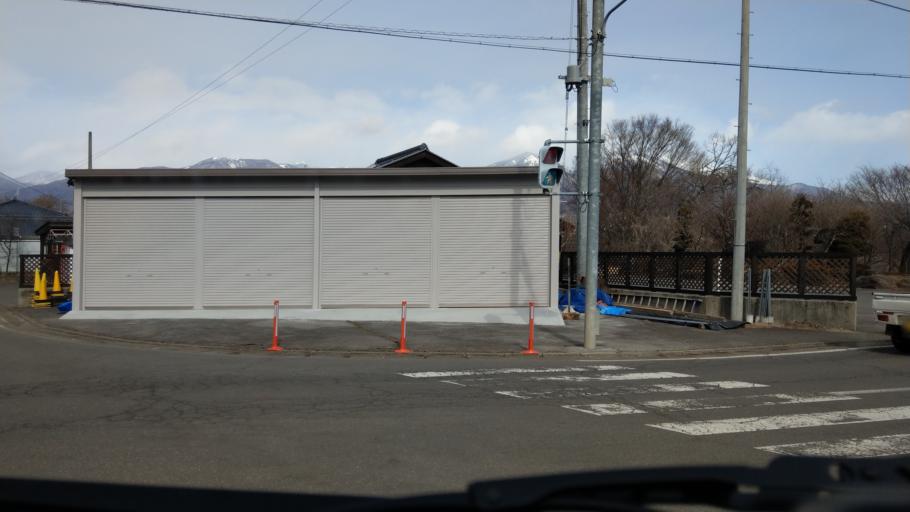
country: JP
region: Nagano
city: Komoro
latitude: 36.3047
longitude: 138.4167
